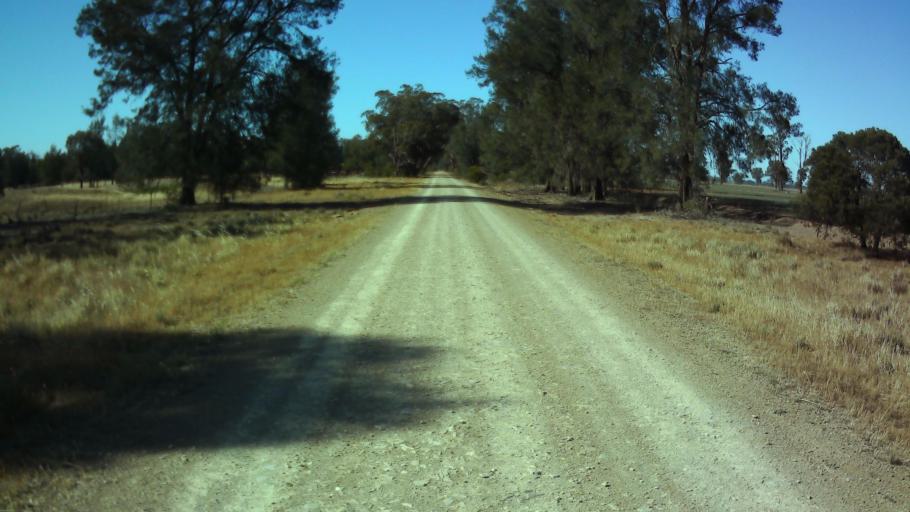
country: AU
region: New South Wales
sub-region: Weddin
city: Grenfell
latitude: -33.9343
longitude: 147.8722
